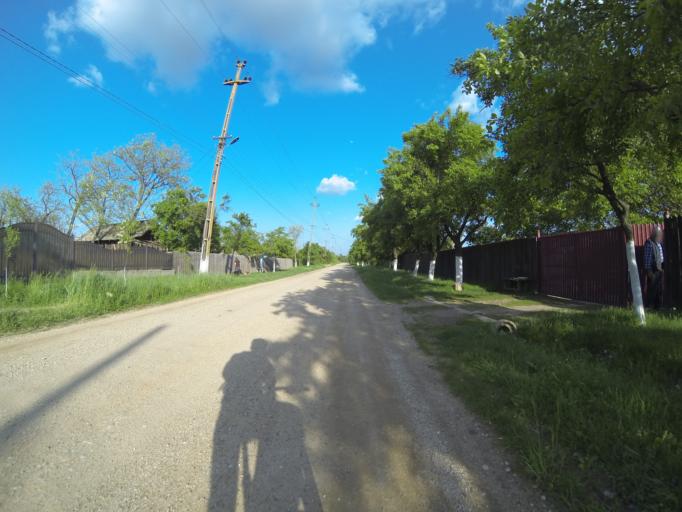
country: RO
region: Dolj
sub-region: Comuna Carpen
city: Carpen
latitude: 44.2951
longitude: 23.2917
